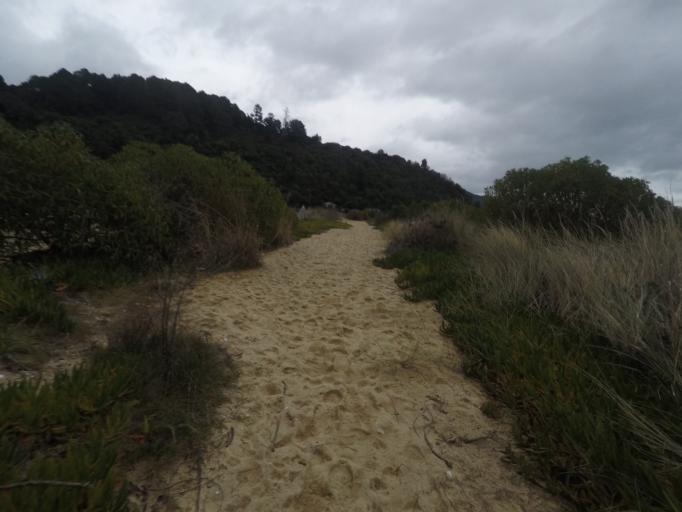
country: NZ
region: Tasman
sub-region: Tasman District
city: Motueka
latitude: -41.0111
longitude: 173.0073
